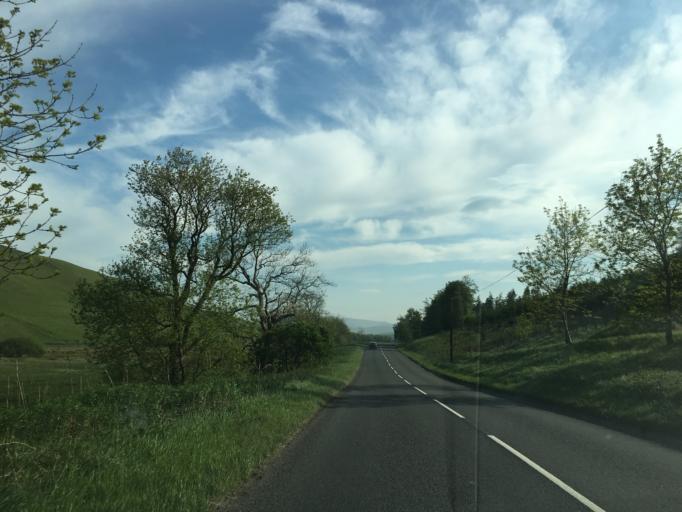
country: GB
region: Scotland
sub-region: South Lanarkshire
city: Biggar
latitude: 55.6609
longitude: -3.4294
